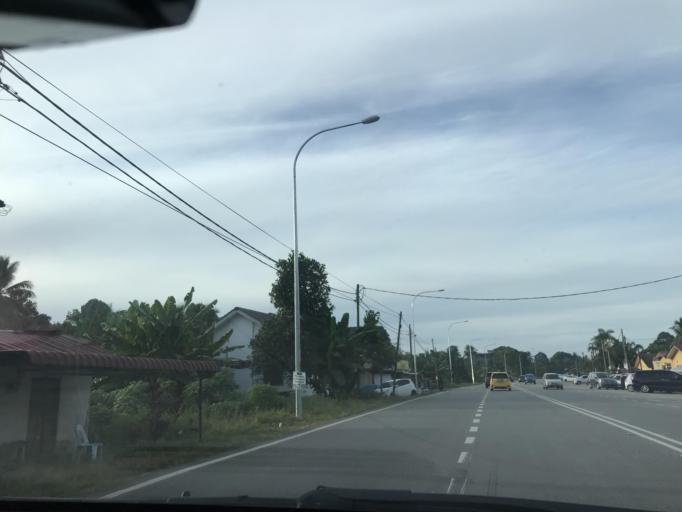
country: MY
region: Kelantan
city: Kampung Lemal
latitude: 5.9953
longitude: 102.1880
